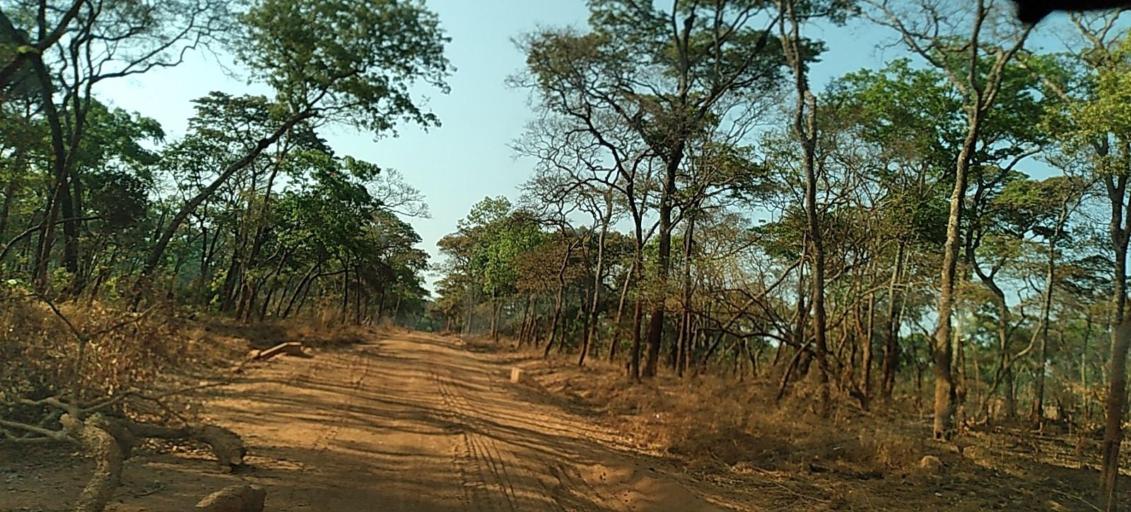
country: ZM
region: North-Western
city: Kasempa
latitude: -13.5549
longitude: 25.9986
